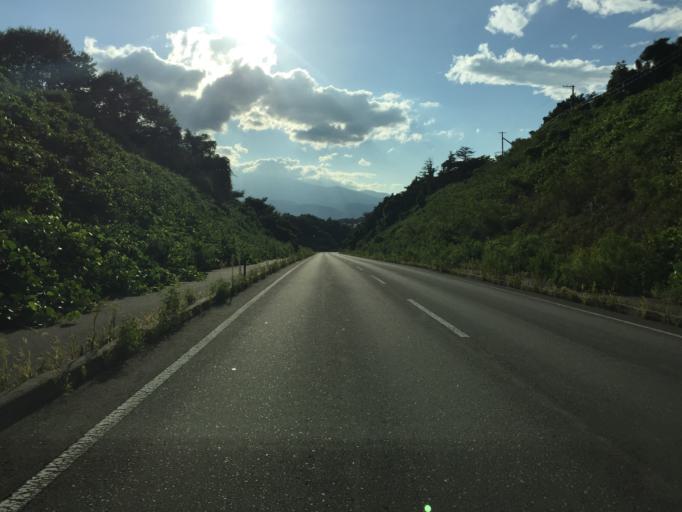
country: JP
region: Fukushima
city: Fukushima-shi
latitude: 37.7231
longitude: 140.4935
